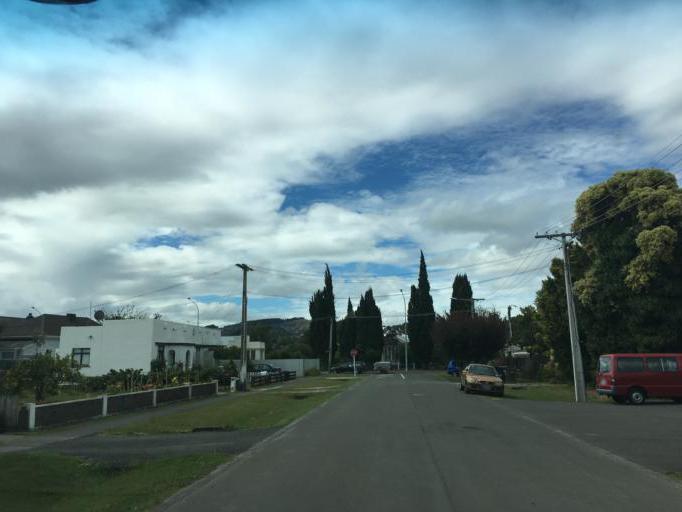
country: NZ
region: Gisborne
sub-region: Gisborne District
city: Gisborne
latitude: -38.6713
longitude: 178.0342
